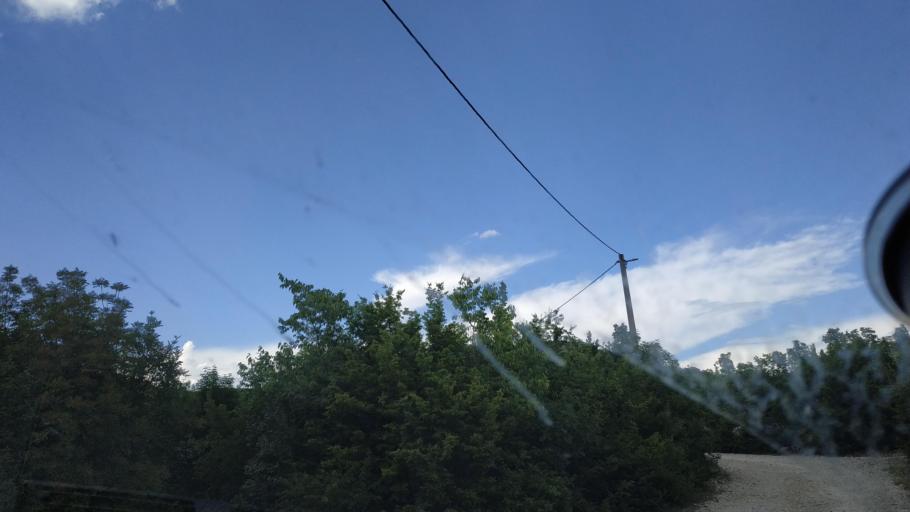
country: HR
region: Splitsko-Dalmatinska
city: Dugopolje
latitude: 43.5627
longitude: 16.6503
